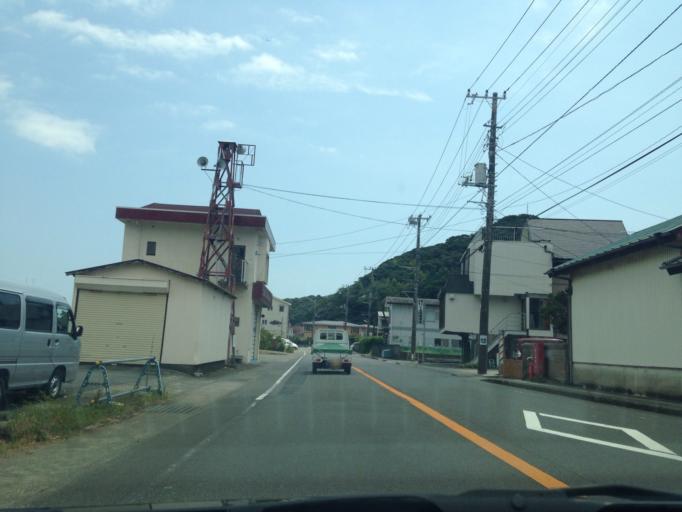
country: JP
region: Shizuoka
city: Shimoda
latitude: 34.6363
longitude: 138.8849
